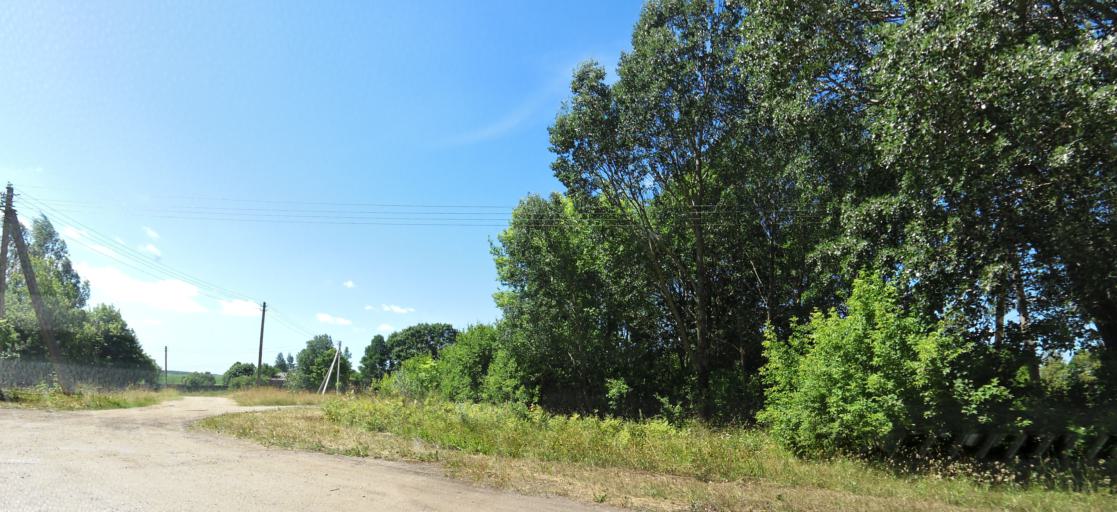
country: LT
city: Vabalninkas
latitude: 55.9407
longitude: 24.8754
